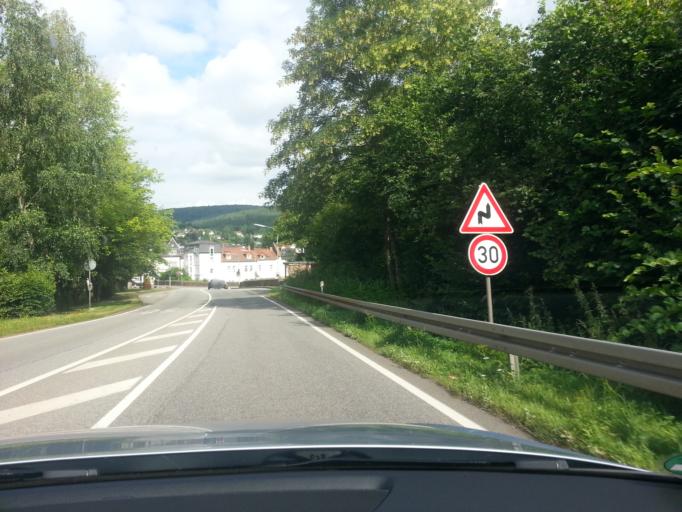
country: DE
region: Saarland
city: Mettlach
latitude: 49.4912
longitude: 6.5945
